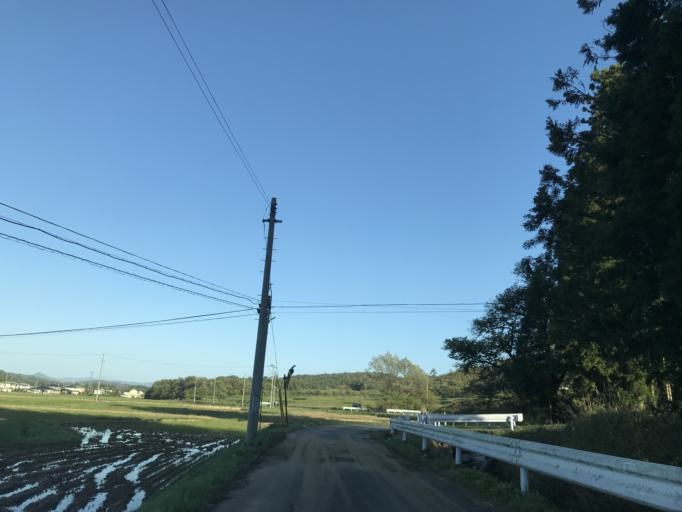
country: JP
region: Iwate
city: Ichinoseki
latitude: 38.9376
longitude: 141.0535
